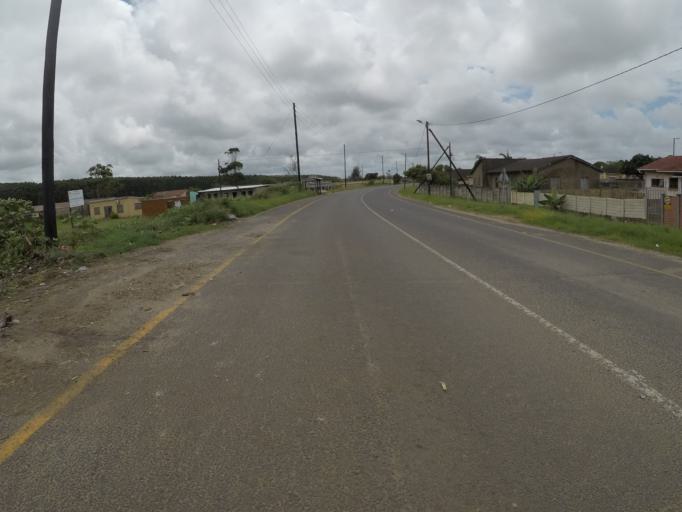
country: ZA
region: KwaZulu-Natal
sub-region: uThungulu District Municipality
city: eSikhawini
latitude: -28.8900
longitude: 31.8812
